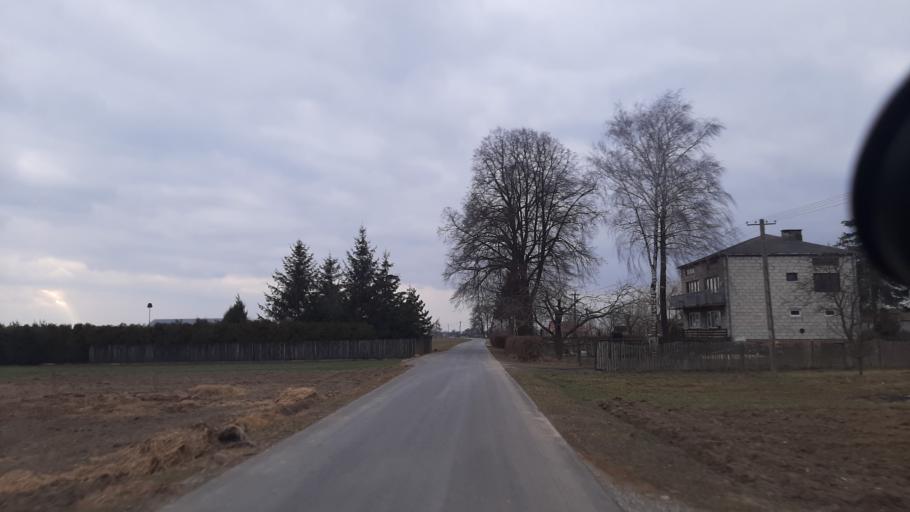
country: PL
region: Lublin Voivodeship
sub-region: Powiat lubelski
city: Jastkow
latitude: 51.3645
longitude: 22.4021
